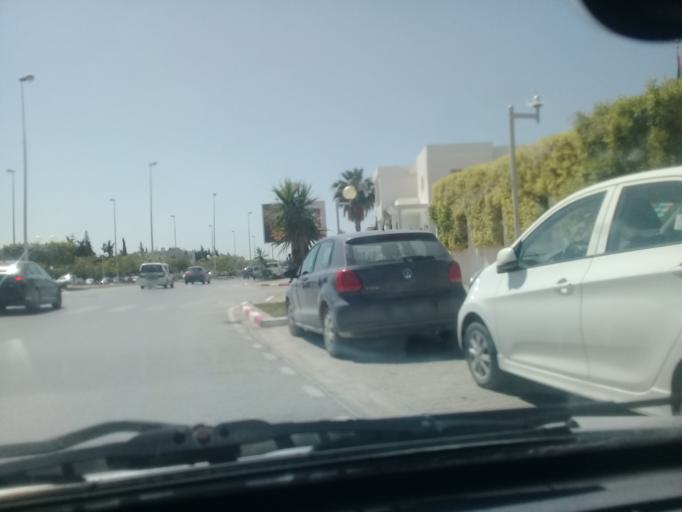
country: TN
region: Ariana
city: Ariana
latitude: 36.8335
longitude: 10.2320
